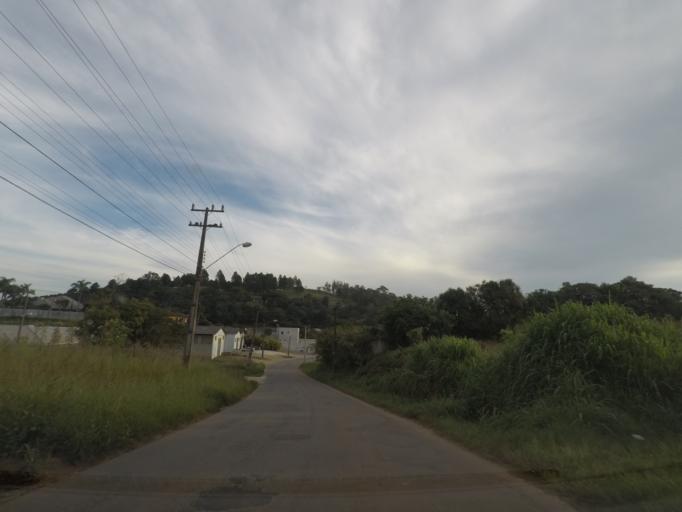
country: BR
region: Parana
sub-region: Colombo
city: Colombo
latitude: -25.2874
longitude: -49.2143
